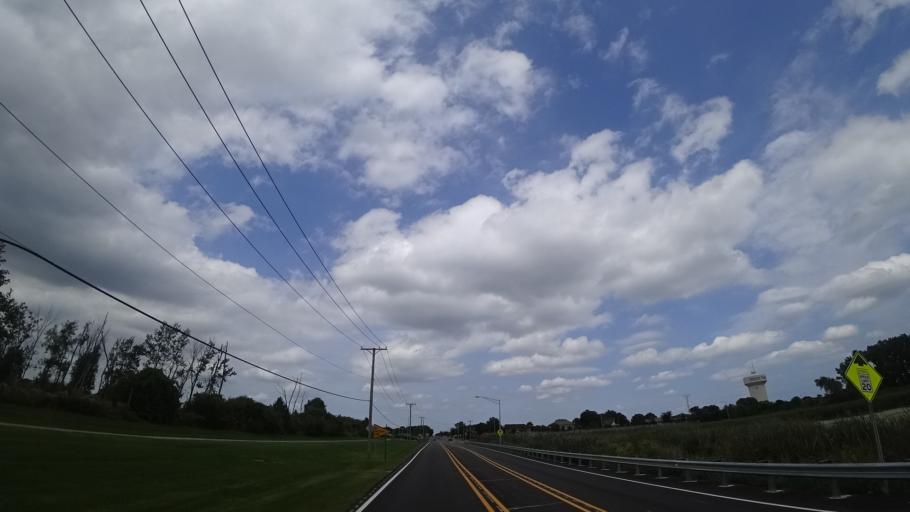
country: US
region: Illinois
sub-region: Cook County
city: Orland Hills
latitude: 41.5640
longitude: -87.8222
